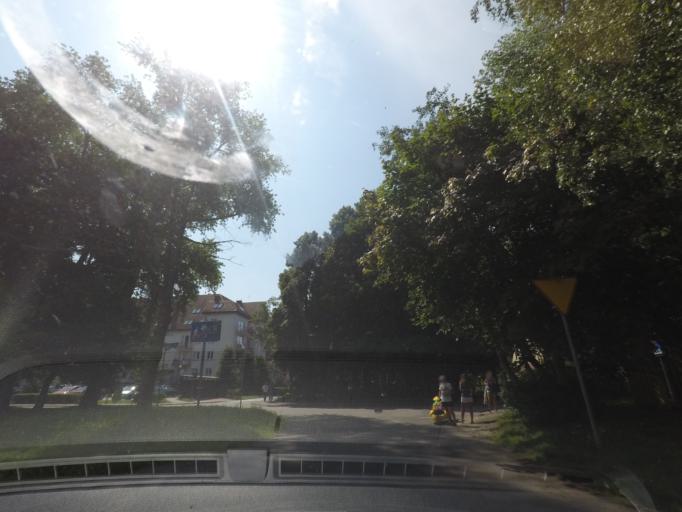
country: PL
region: West Pomeranian Voivodeship
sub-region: Powiat kolobrzeski
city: Dygowo
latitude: 54.1927
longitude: 15.6662
